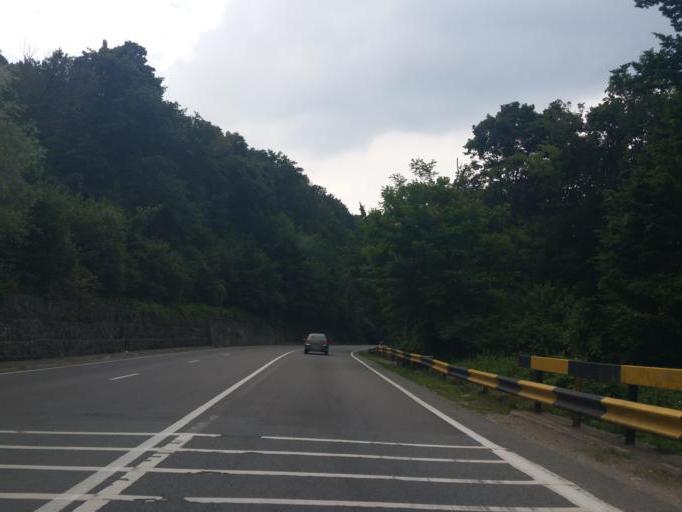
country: RO
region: Salaj
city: Zalau
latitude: 47.1557
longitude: 23.0915
